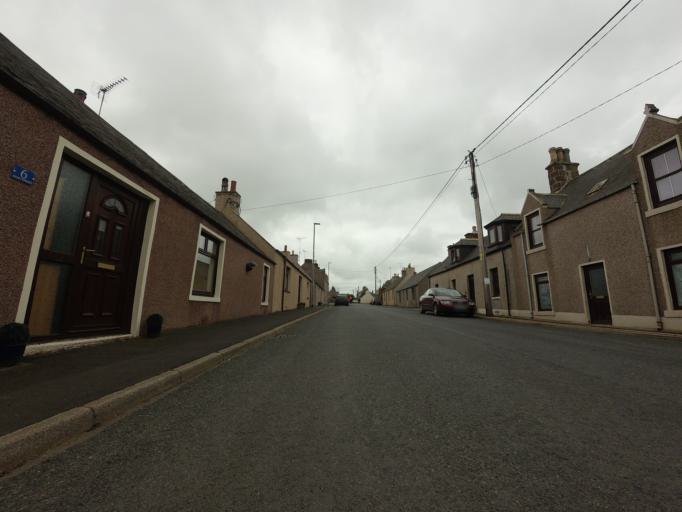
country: GB
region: Scotland
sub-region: Aberdeenshire
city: Turriff
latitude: 57.5433
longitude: -2.3355
